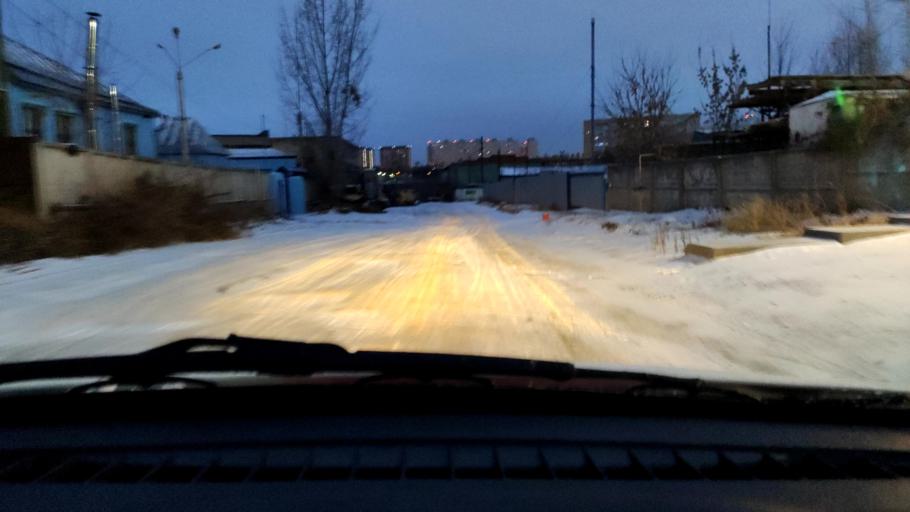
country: RU
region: Voronezj
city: Voronezh
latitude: 51.6848
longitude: 39.1469
